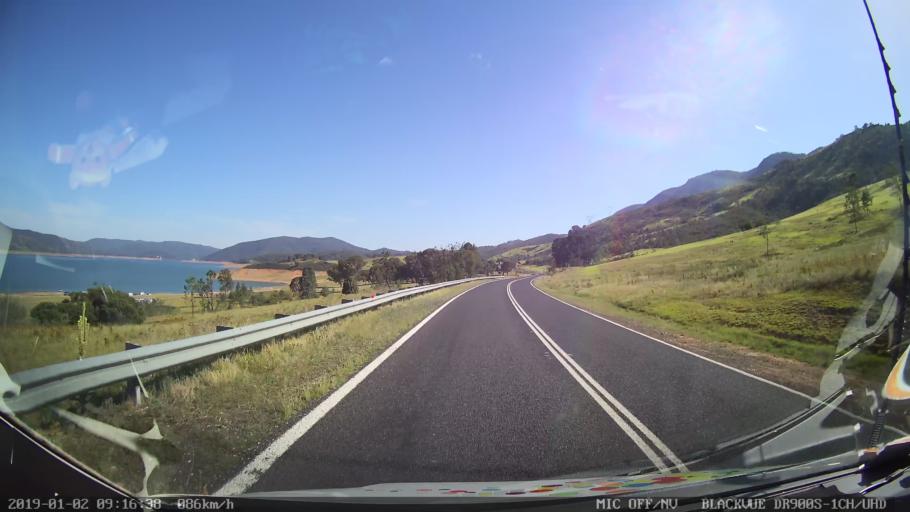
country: AU
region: New South Wales
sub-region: Tumut Shire
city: Tumut
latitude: -35.4509
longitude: 148.2845
